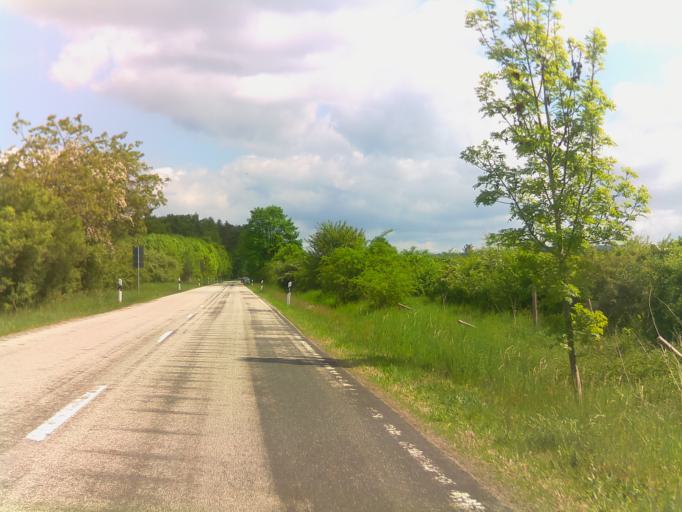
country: DE
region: Thuringia
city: Vachdorf
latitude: 50.5401
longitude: 10.5460
